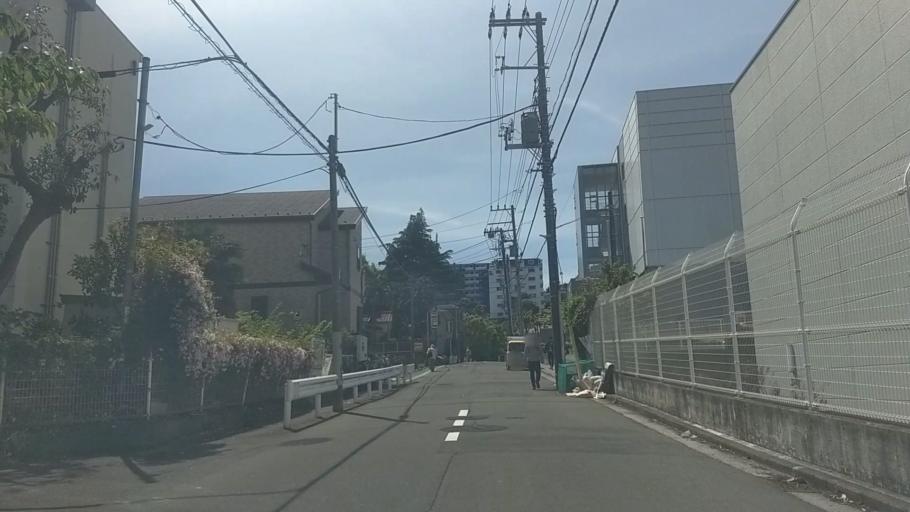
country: JP
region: Kanagawa
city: Yokohama
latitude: 35.4319
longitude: 139.6284
